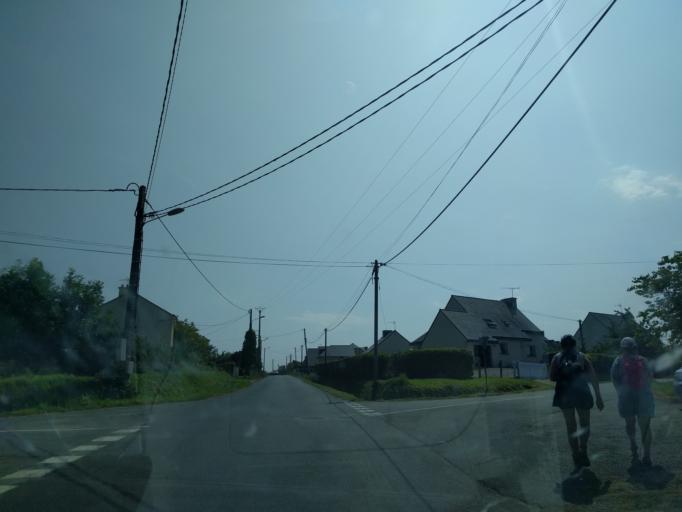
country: FR
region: Brittany
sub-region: Departement des Cotes-d'Armor
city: Plurien
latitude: 48.6412
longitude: -2.4246
